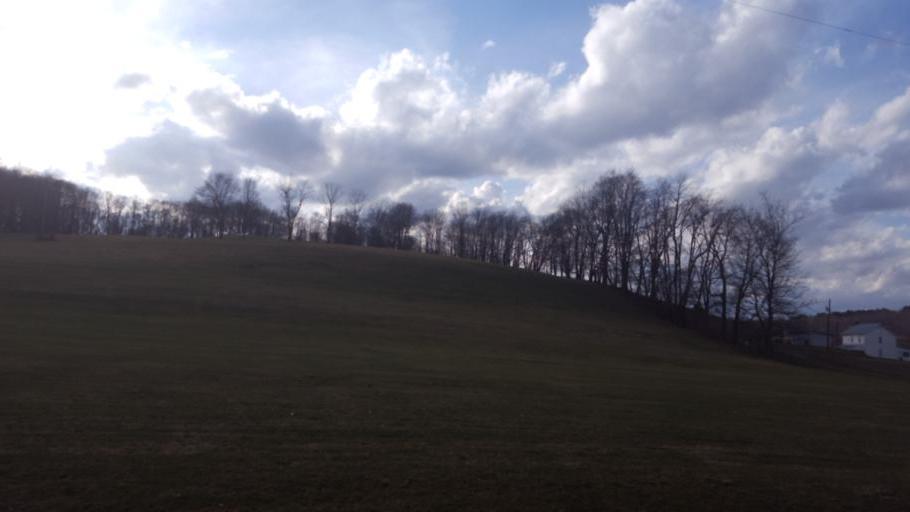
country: US
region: Ohio
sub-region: Sandusky County
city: Bellville
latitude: 40.5718
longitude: -82.4369
